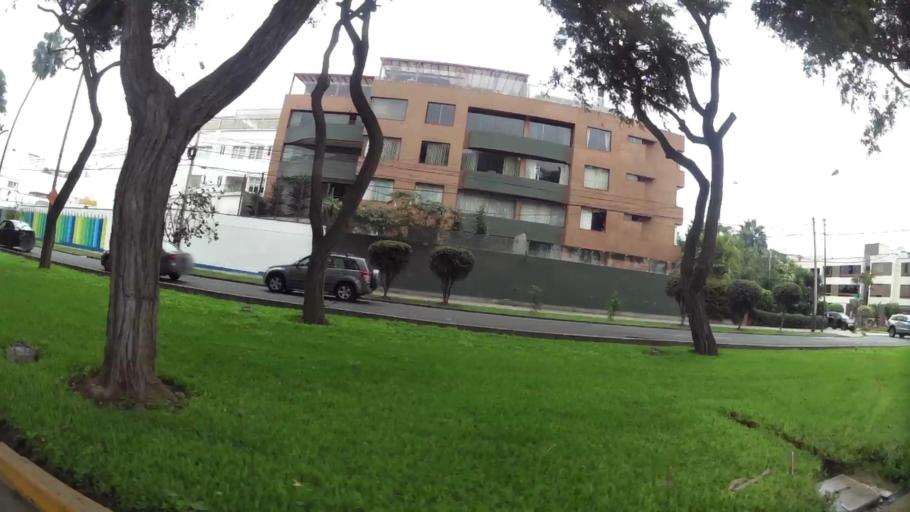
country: PE
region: Lima
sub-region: Lima
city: Surco
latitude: -12.1173
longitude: -76.9840
